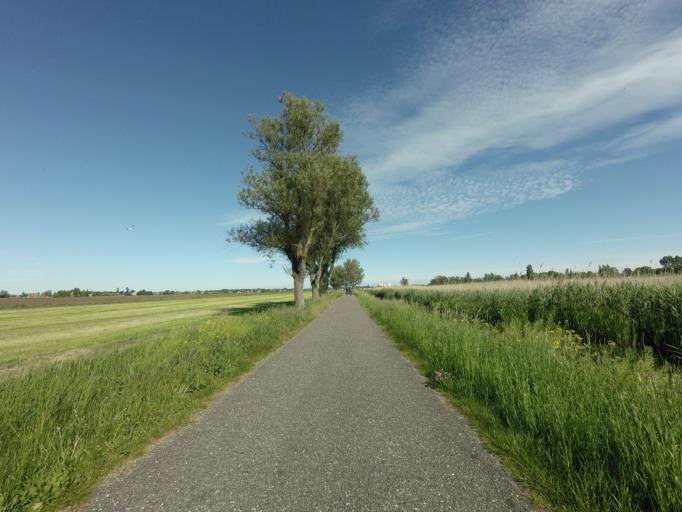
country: NL
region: North Holland
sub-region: Gemeente Uitgeest
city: Uitgeest
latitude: 52.5131
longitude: 4.7514
